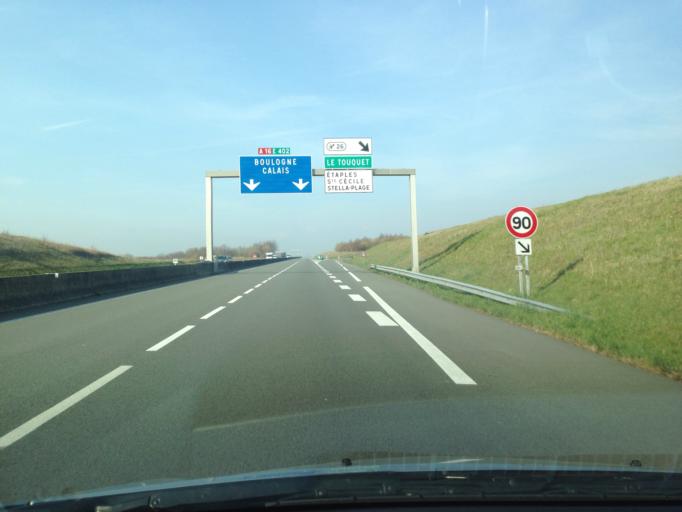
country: FR
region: Nord-Pas-de-Calais
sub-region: Departement du Pas-de-Calais
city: Saint-Josse
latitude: 50.5059
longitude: 1.6823
